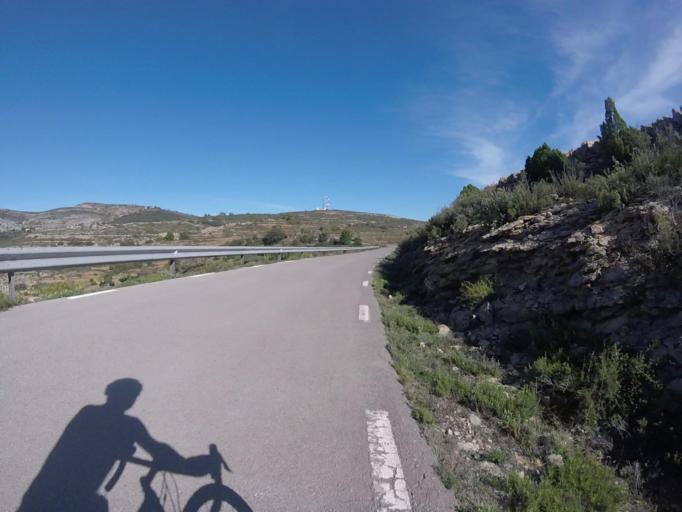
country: ES
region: Valencia
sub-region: Provincia de Castello
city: Sarratella
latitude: 40.2944
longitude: 0.0308
